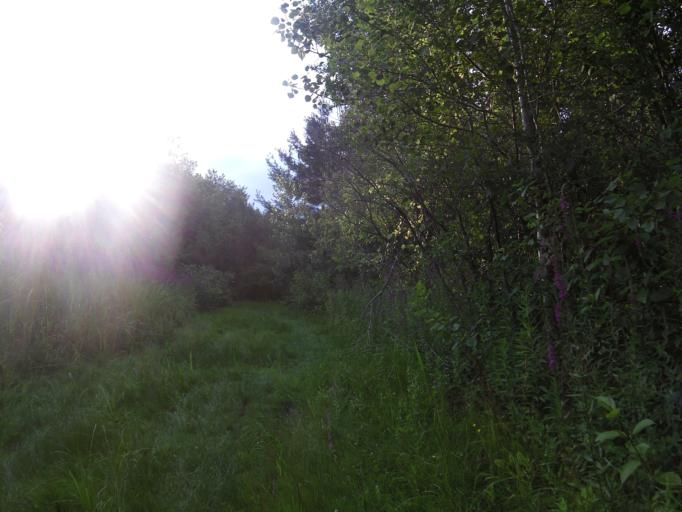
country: CA
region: Ontario
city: Bells Corners
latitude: 45.2944
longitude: -75.9060
